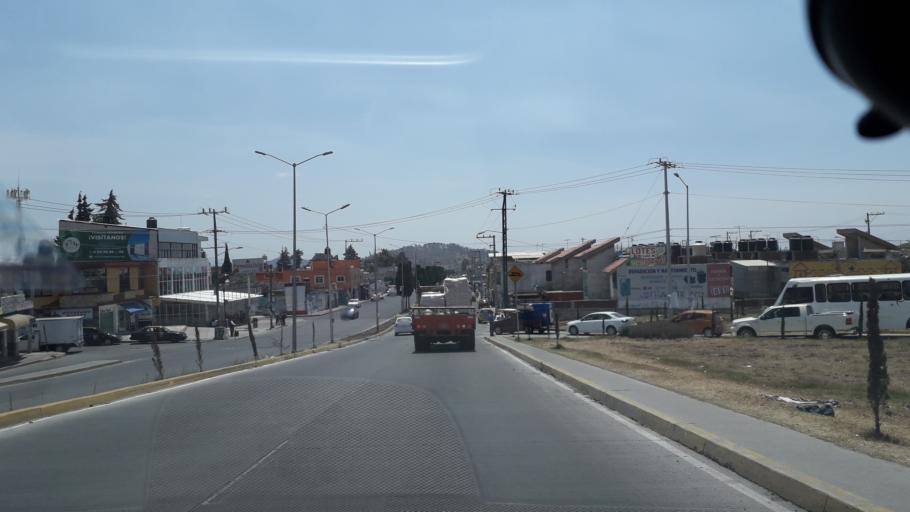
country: MX
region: Puebla
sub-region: Amozoc
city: Casa Blanca
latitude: 19.0667
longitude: -98.1198
